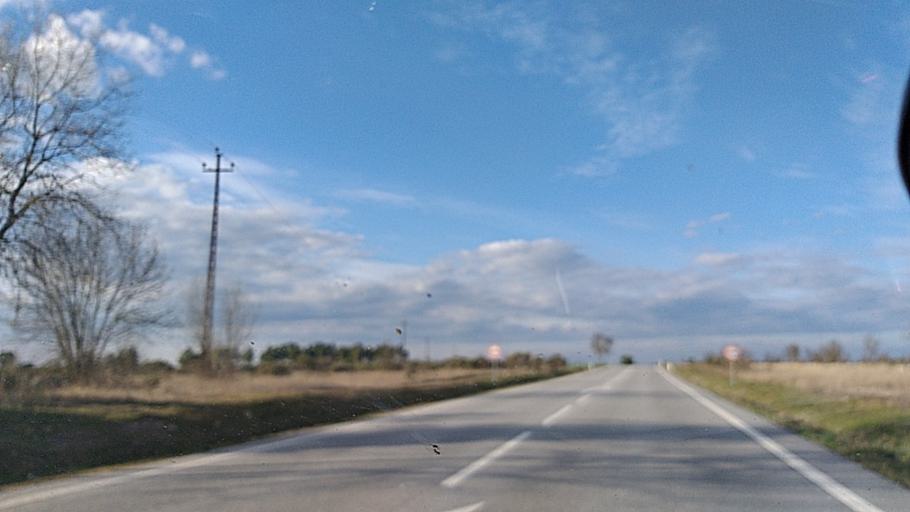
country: ES
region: Castille and Leon
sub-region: Provincia de Salamanca
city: Fuentes de Onoro
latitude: 40.6495
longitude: -6.8568
